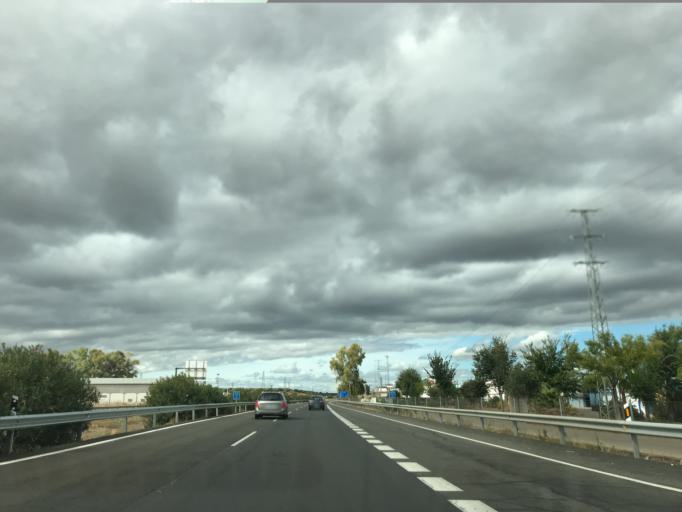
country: ES
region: Andalusia
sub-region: Province of Cordoba
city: Villa del Rio
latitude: 37.9866
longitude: -4.3052
